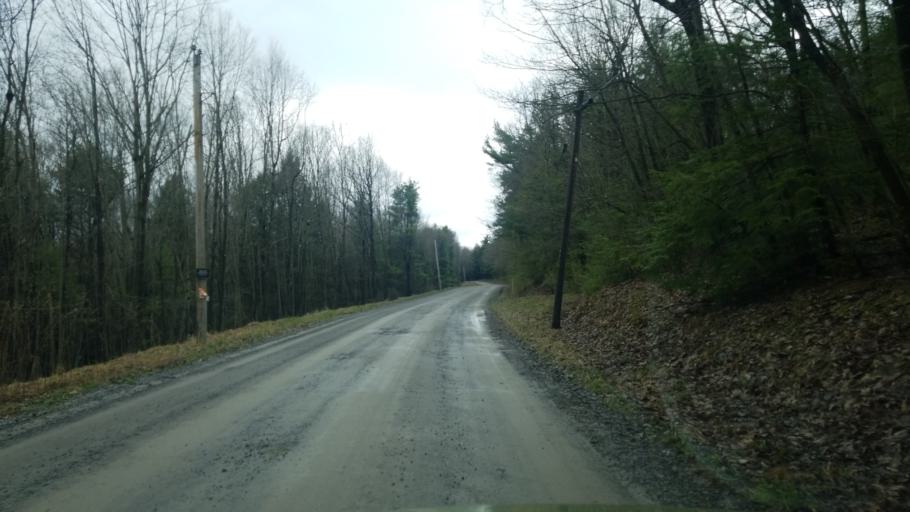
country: US
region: Pennsylvania
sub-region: Clearfield County
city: Shiloh
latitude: 41.1356
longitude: -78.3343
